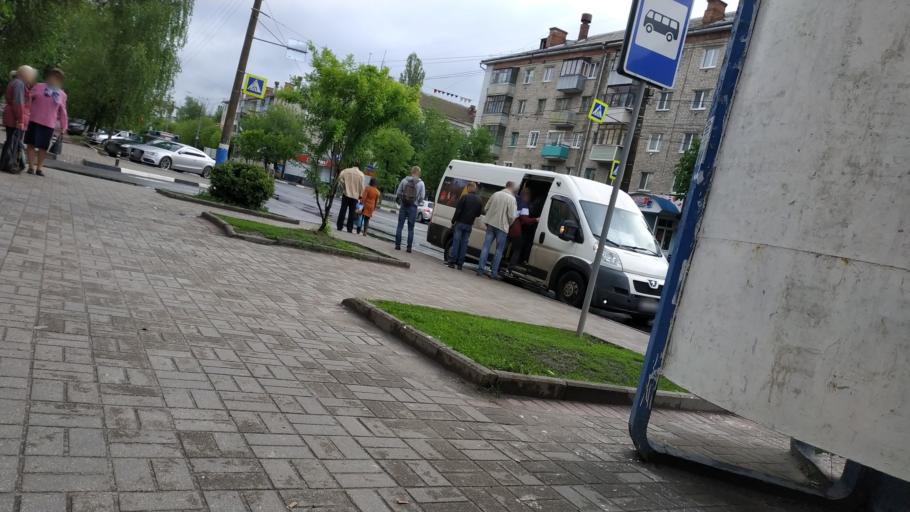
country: RU
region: Brjansk
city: Putevka
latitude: 53.3050
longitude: 34.3013
